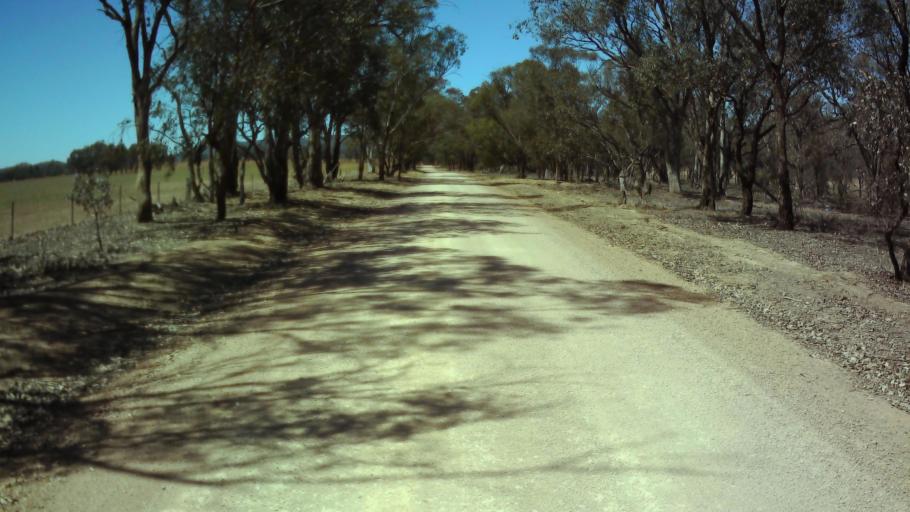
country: AU
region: New South Wales
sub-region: Weddin
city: Grenfell
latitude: -33.9242
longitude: 148.0784
